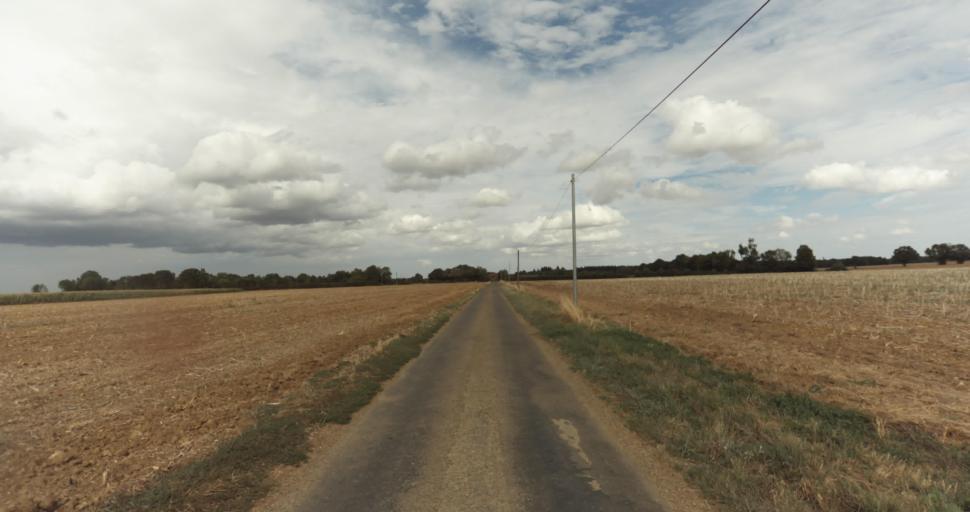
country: FR
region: Lower Normandy
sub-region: Departement de l'Orne
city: Gace
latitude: 48.8798
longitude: 0.3592
